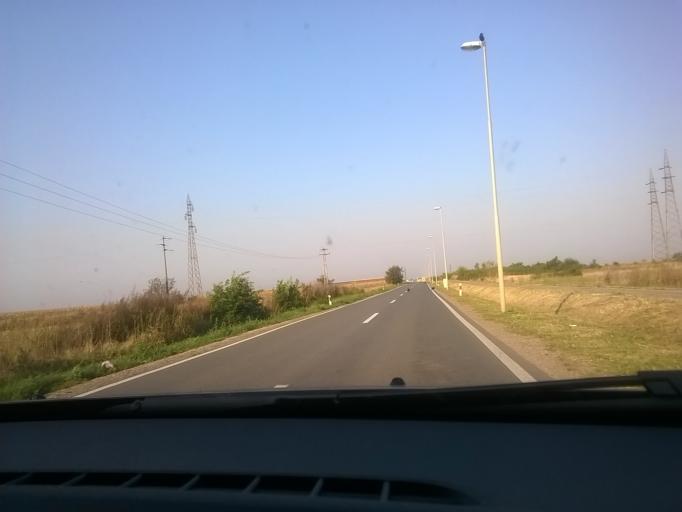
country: RS
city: Pavlis
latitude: 45.1126
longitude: 21.2709
